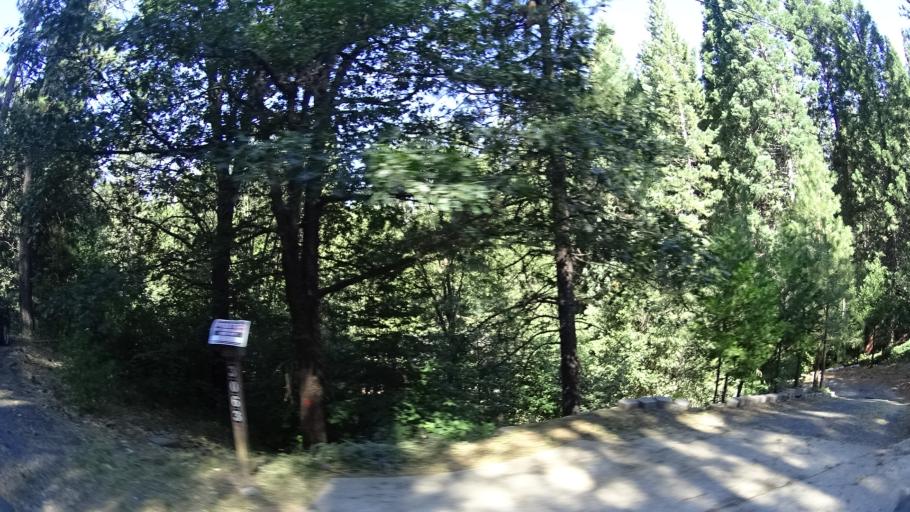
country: US
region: California
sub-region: Calaveras County
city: Arnold
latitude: 38.2543
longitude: -120.3668
